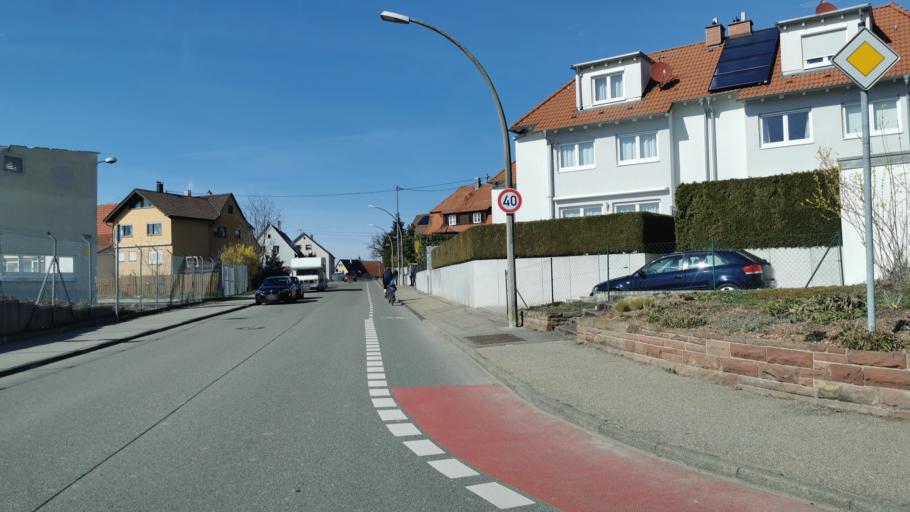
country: DE
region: Baden-Wuerttemberg
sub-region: Regierungsbezirk Stuttgart
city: Rutesheim
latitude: 48.8055
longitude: 8.9509
